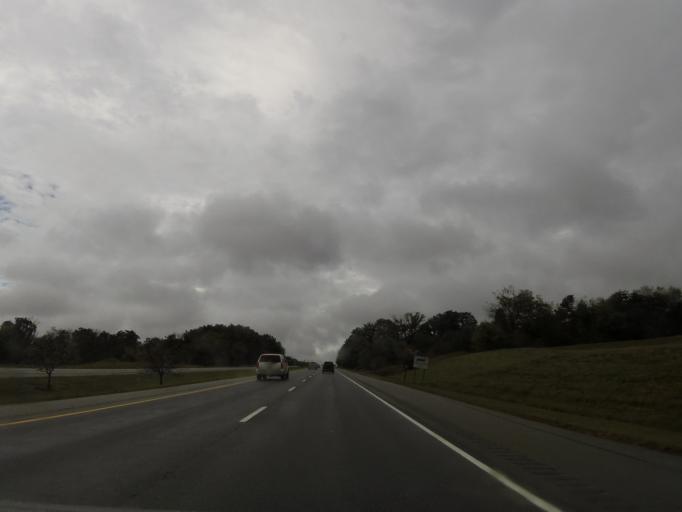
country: US
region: Tennessee
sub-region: Blount County
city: Louisville
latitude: 35.7566
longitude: -84.0391
